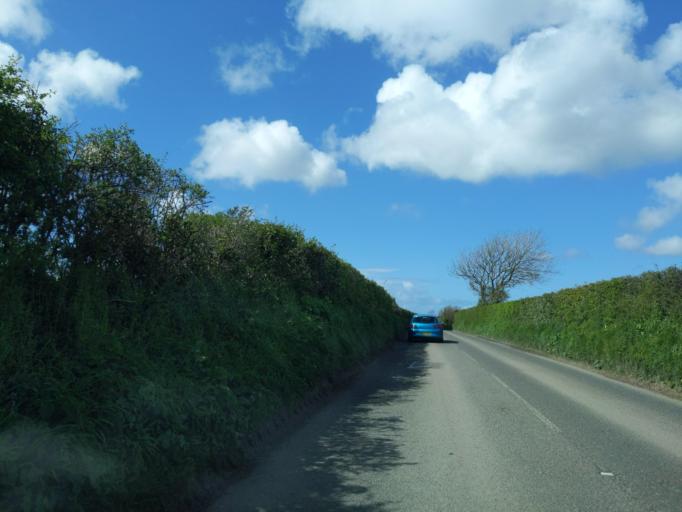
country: GB
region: England
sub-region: Cornwall
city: Wadebridge
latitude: 50.5299
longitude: -4.8353
